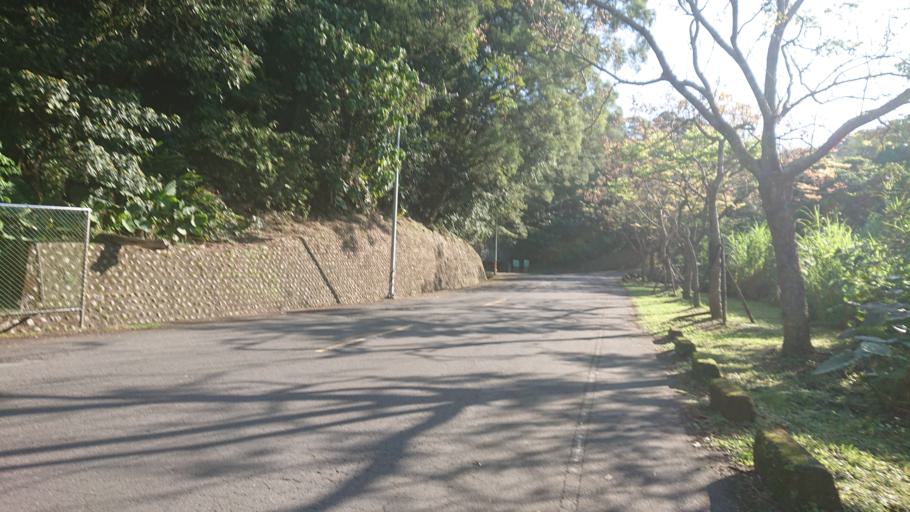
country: TW
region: Taipei
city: Taipei
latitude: 24.9790
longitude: 121.5713
